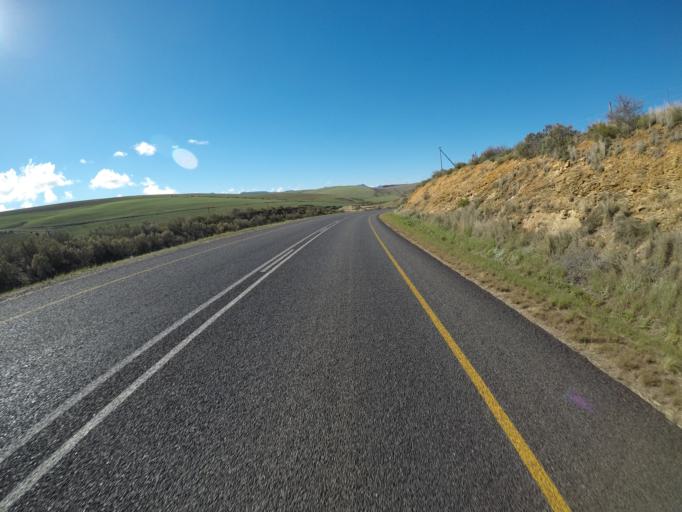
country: ZA
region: Western Cape
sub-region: Overberg District Municipality
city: Caledon
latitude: -34.1517
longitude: 19.4745
